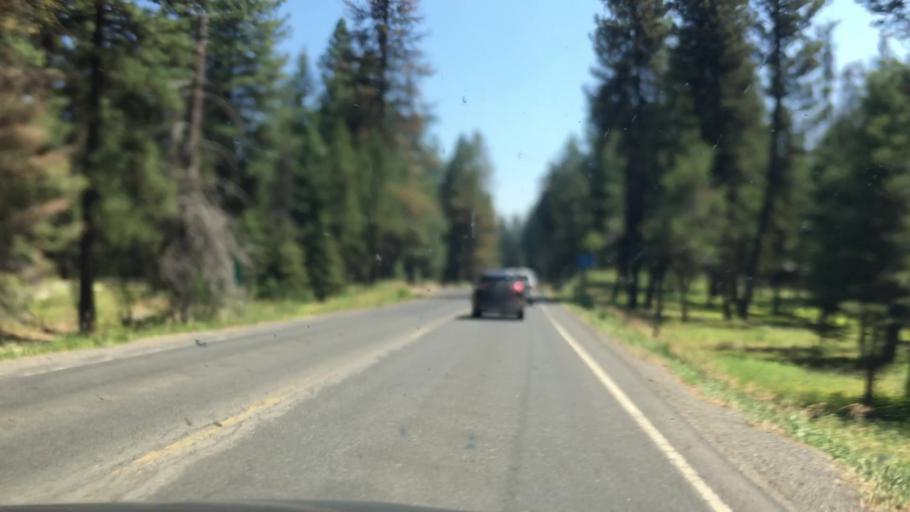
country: US
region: Idaho
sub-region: Valley County
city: McCall
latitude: 44.9189
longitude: -116.1358
